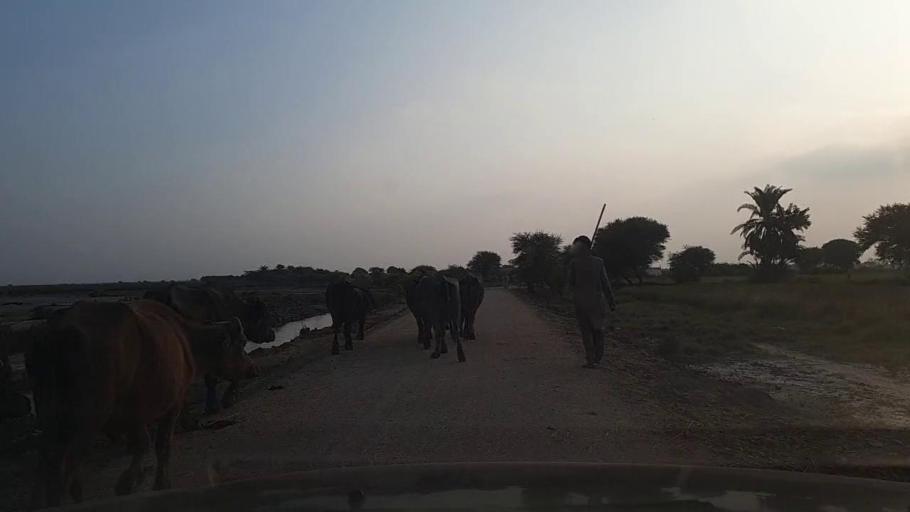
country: PK
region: Sindh
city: Jati
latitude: 24.5337
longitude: 68.3579
